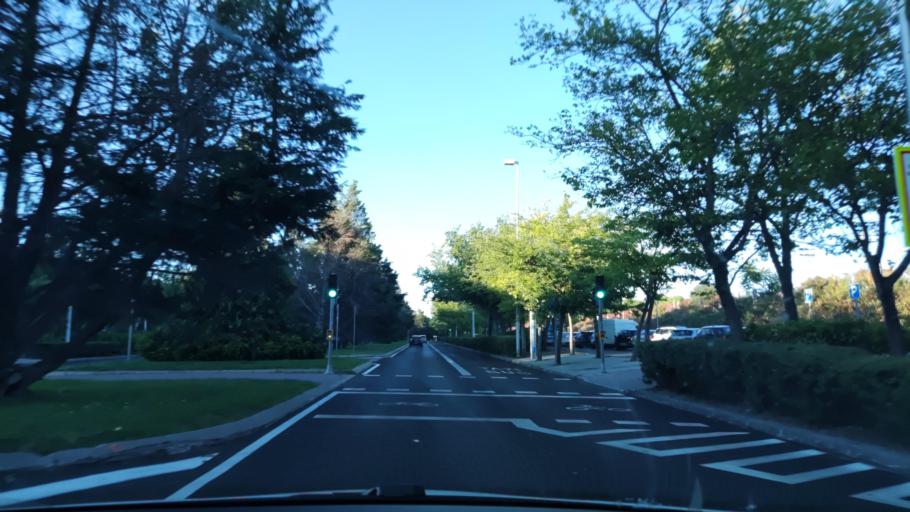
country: ES
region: Madrid
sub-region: Provincia de Madrid
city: Carabanchel
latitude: 40.3806
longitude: -3.7254
